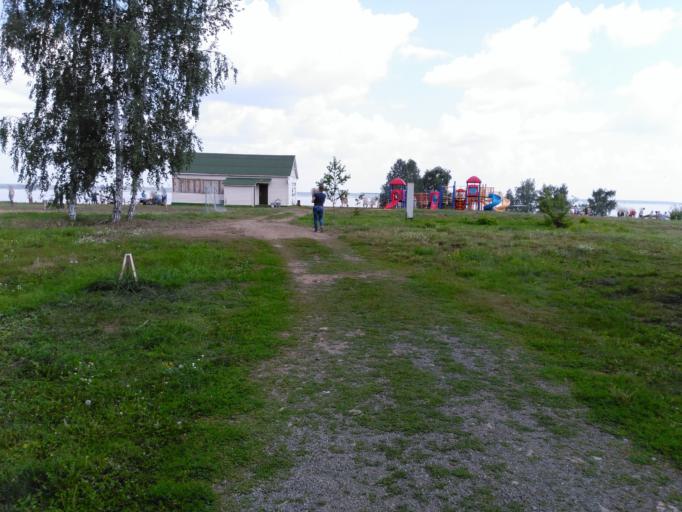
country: RU
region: Chelyabinsk
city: Kunashak
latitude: 55.6647
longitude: 61.2725
